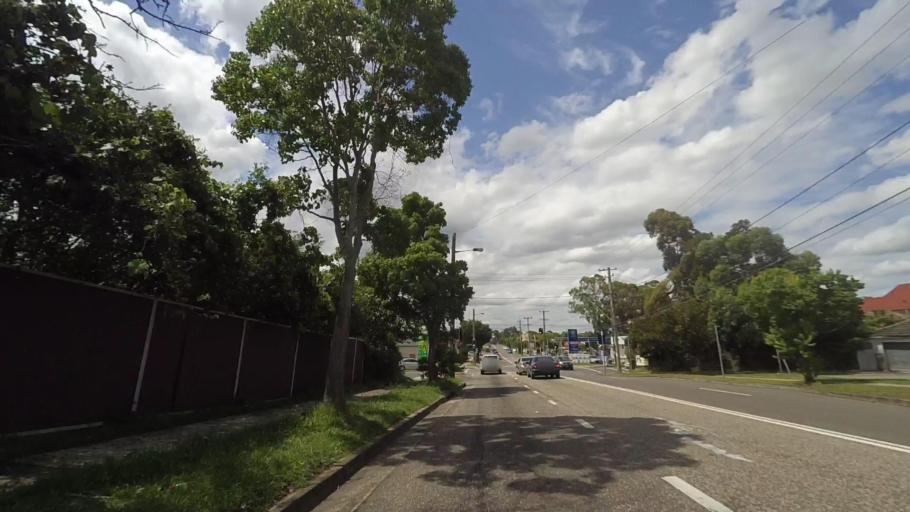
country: AU
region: New South Wales
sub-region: Fairfield
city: Fairfield Heights
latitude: -33.8734
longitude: 150.9452
